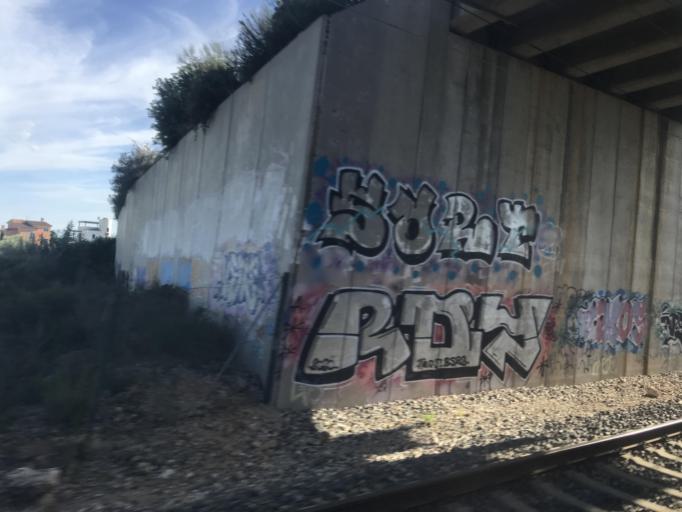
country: ES
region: Catalonia
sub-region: Provincia de Tarragona
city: L'Ampolla
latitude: 40.8178
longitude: 0.7180
